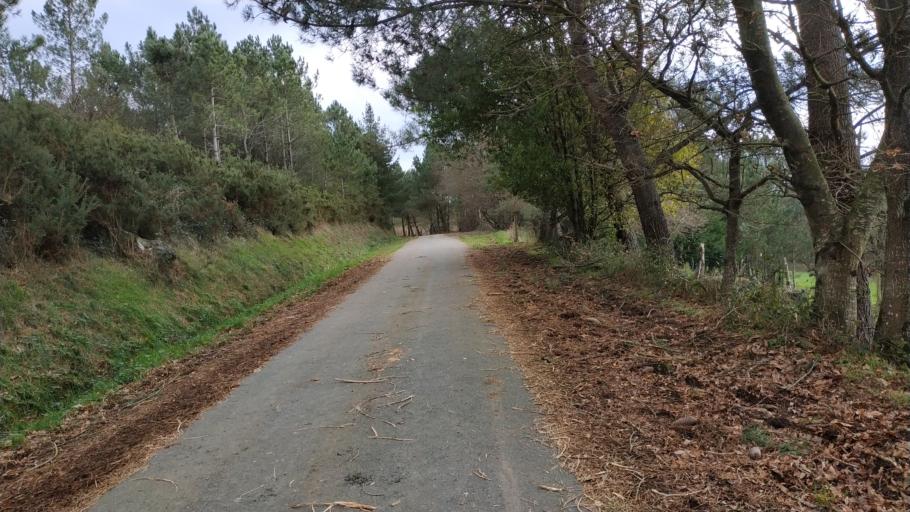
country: ES
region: Galicia
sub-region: Provincia de Pontevedra
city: Silleda
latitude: 42.7724
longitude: -8.1664
